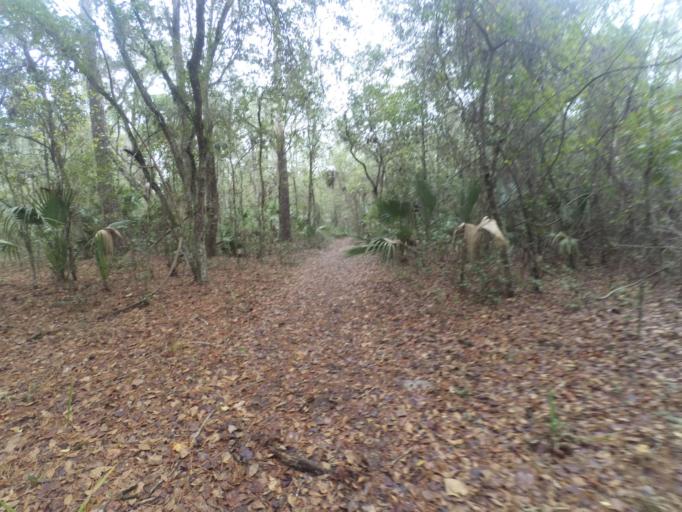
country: US
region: Florida
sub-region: Alachua County
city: Gainesville
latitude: 29.5417
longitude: -82.2728
